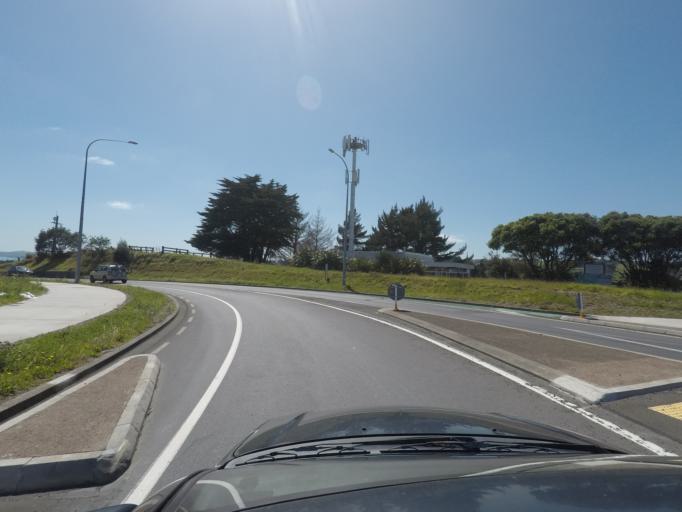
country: NZ
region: Auckland
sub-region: Auckland
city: Pakuranga
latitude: -36.8899
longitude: 175.0129
